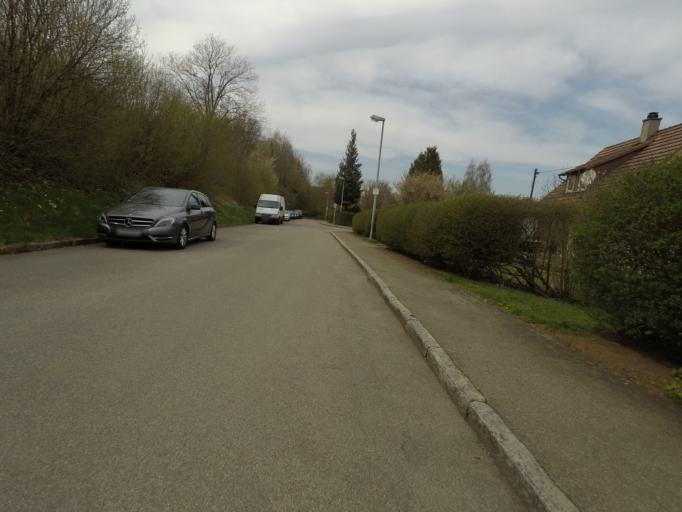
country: DE
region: Baden-Wuerttemberg
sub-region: Tuebingen Region
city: Gomaringen
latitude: 48.4505
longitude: 9.1351
